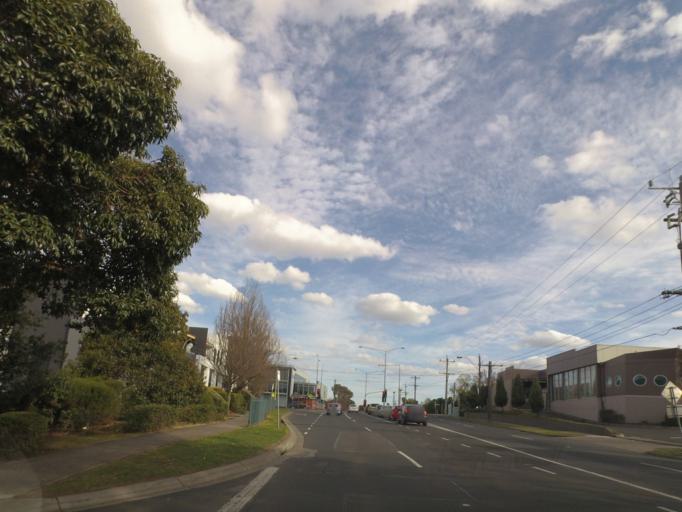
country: AU
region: Victoria
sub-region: Manningham
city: Doncaster East
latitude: -37.7861
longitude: 145.1439
